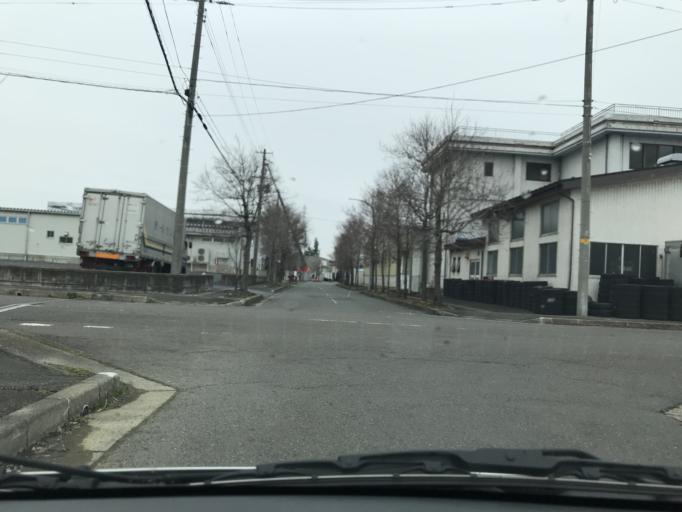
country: JP
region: Iwate
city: Mizusawa
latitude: 39.1783
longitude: 141.1124
